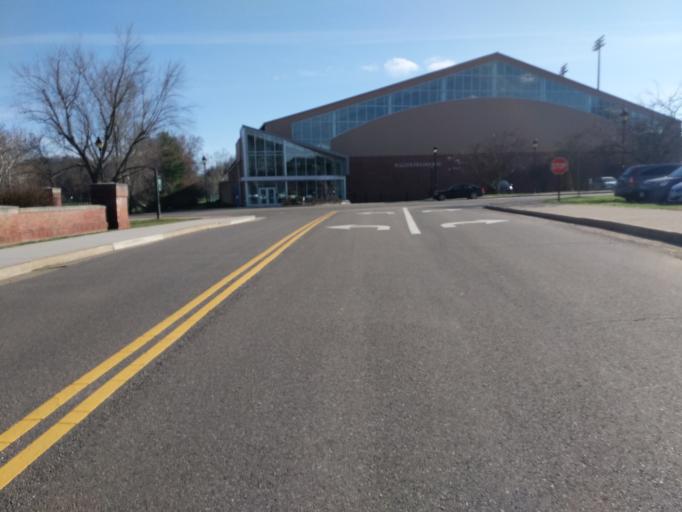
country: US
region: Ohio
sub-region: Athens County
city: Athens
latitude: 39.3223
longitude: -82.1012
